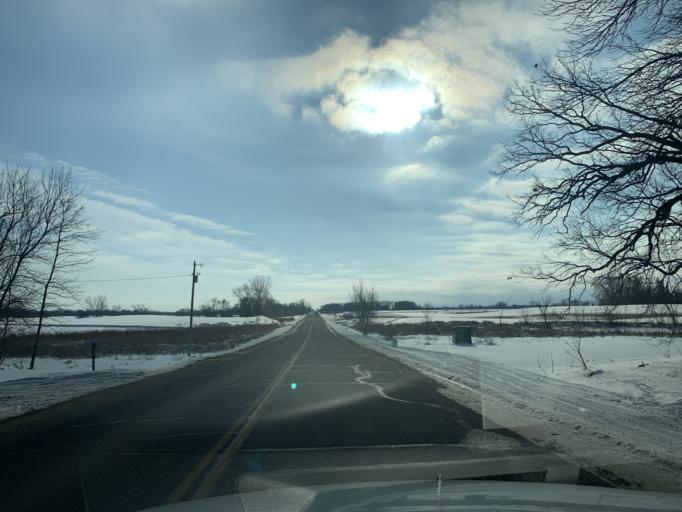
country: US
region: Minnesota
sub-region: Wright County
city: Buffalo
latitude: 45.1980
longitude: -93.8271
